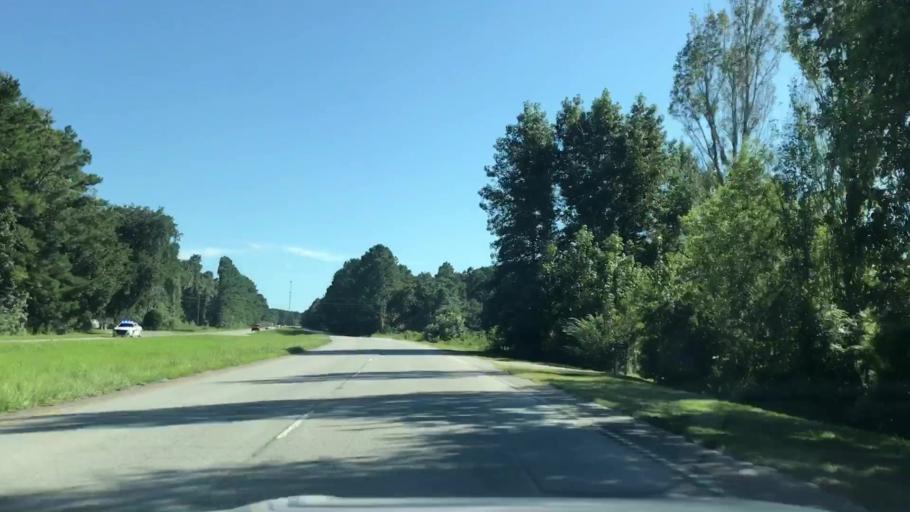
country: US
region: South Carolina
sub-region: Charleston County
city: Awendaw
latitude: 33.0024
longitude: -79.6435
